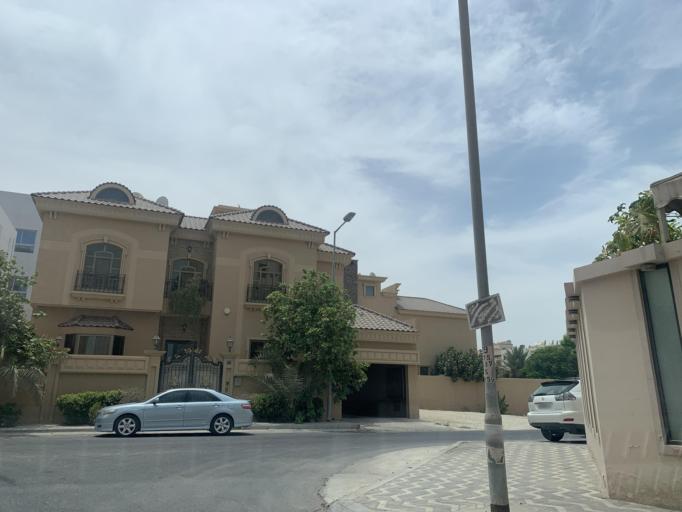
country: BH
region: Northern
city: Madinat `Isa
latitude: 26.1806
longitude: 50.4797
